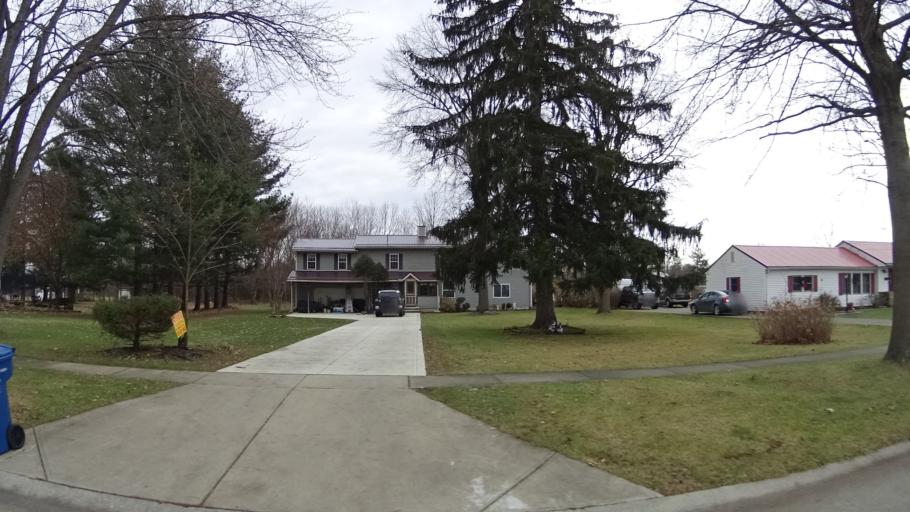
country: US
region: Ohio
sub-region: Lorain County
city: Wellington
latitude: 41.1664
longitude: -82.2102
